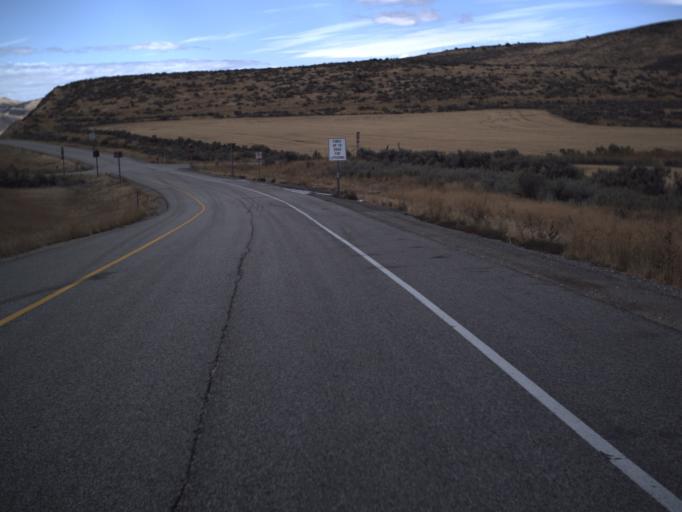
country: US
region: Utah
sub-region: Box Elder County
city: Garland
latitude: 41.8977
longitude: -112.5425
